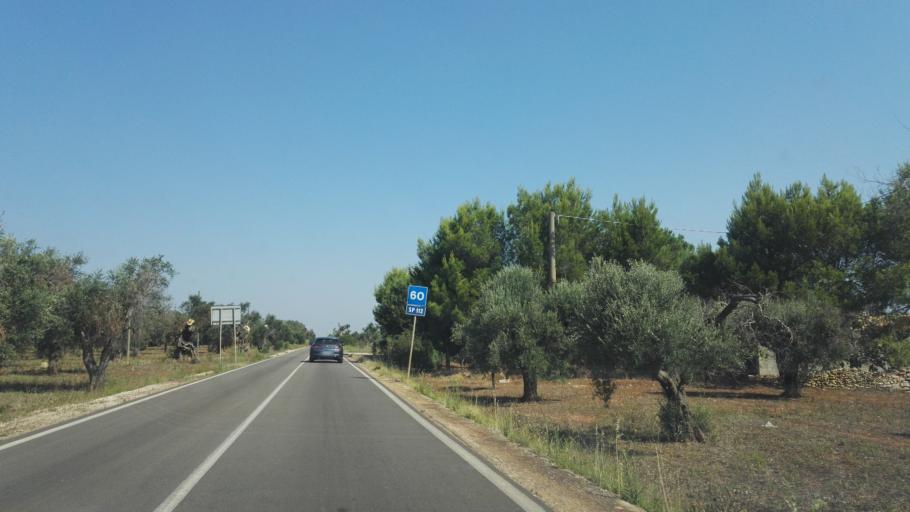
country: IT
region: Apulia
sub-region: Provincia di Lecce
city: Nardo
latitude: 40.1769
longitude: 17.9780
